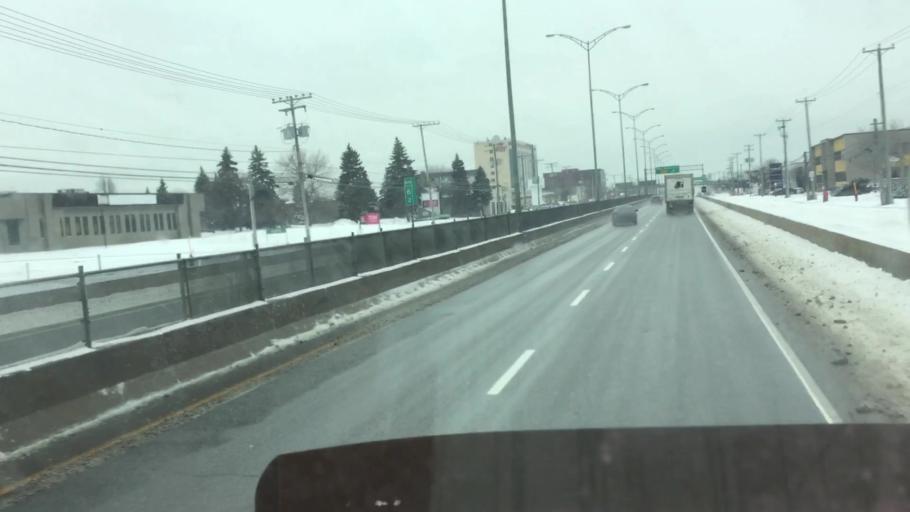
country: CA
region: Quebec
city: Saint-Laurent
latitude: 45.4876
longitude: -73.6893
